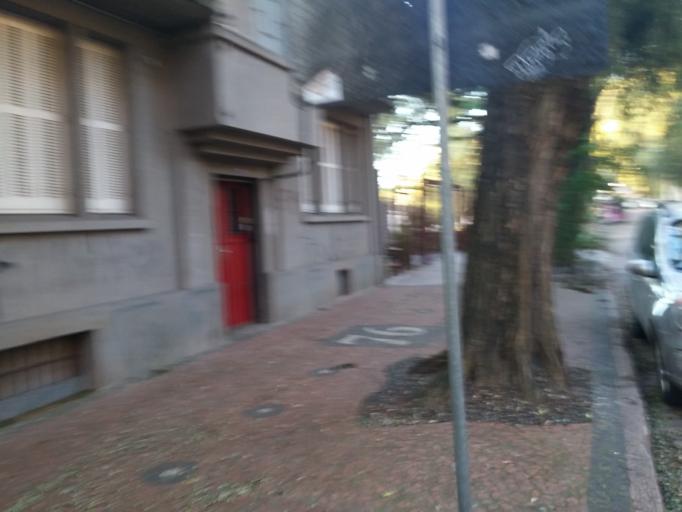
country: BR
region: Rio Grande do Sul
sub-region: Porto Alegre
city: Porto Alegre
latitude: -30.0279
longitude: -51.2135
